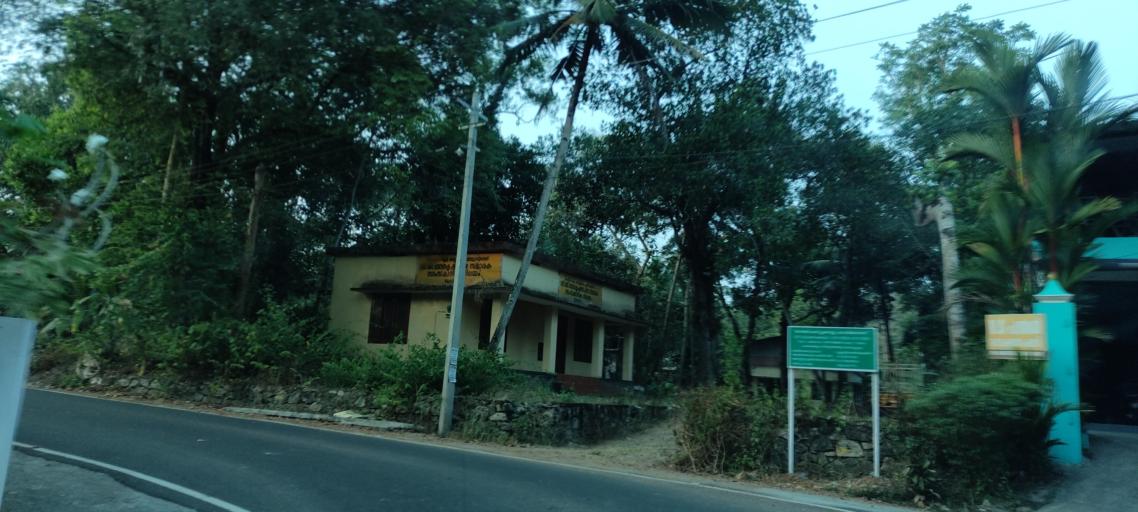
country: IN
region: Kerala
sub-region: Alappuzha
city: Mavelikara
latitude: 9.2786
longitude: 76.5545
